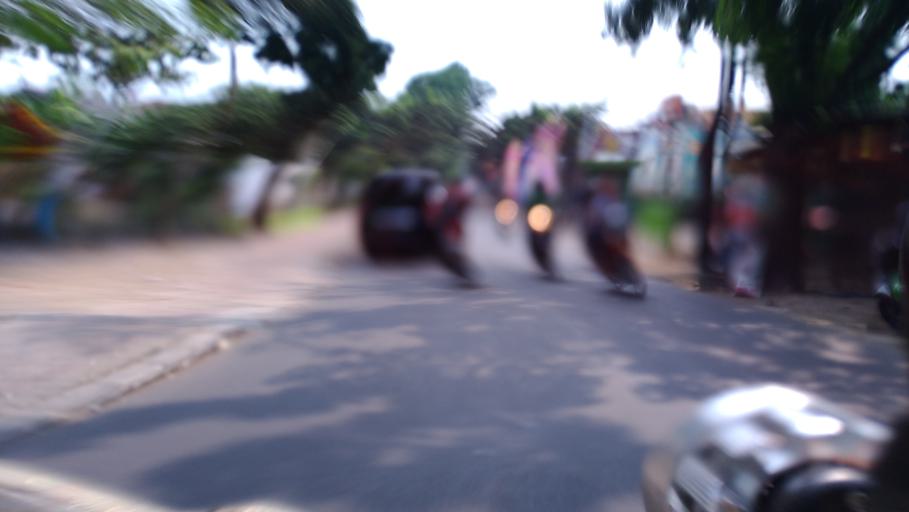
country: ID
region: West Java
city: Depok
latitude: -6.3521
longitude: 106.8866
